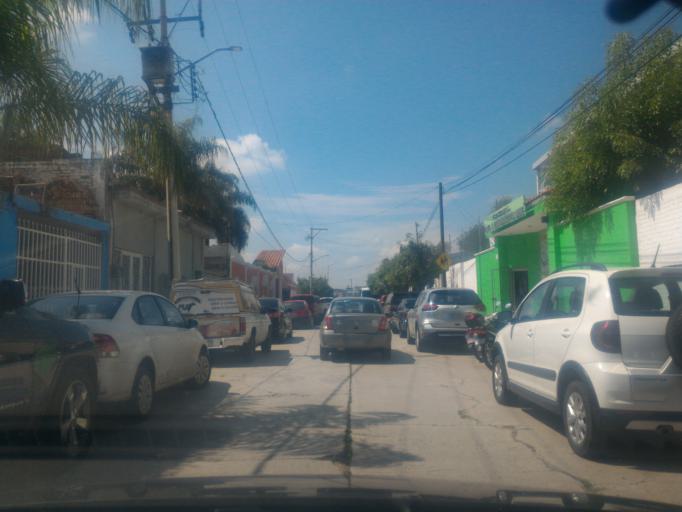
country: MX
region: Guanajuato
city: San Francisco del Rincon
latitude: 21.0102
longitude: -101.8631
